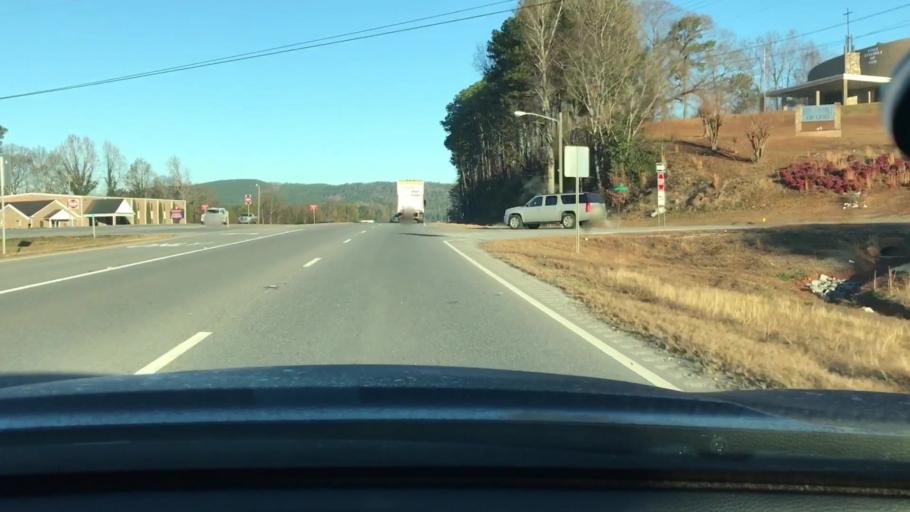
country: US
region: Alabama
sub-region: Talladega County
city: Mignon
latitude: 33.1819
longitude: -86.2999
